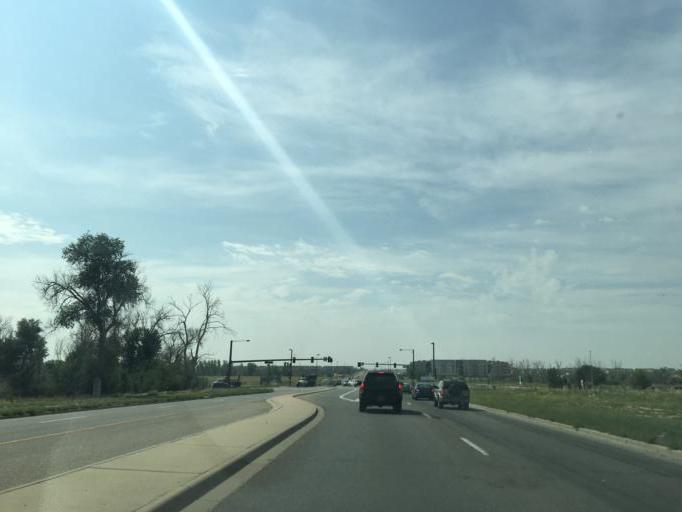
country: US
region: Colorado
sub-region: Adams County
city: Aurora
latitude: 39.7998
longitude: -104.7722
